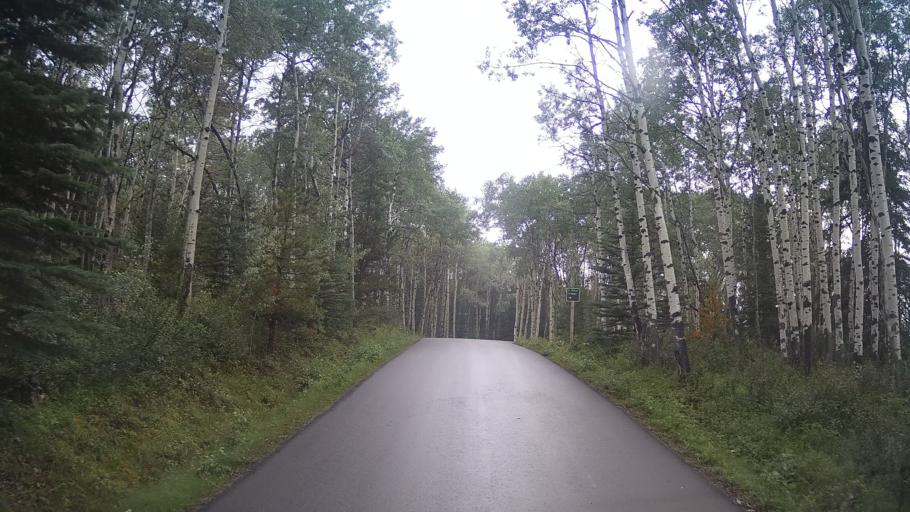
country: CA
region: Alberta
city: Jasper Park Lodge
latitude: 52.9137
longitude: -118.0959
